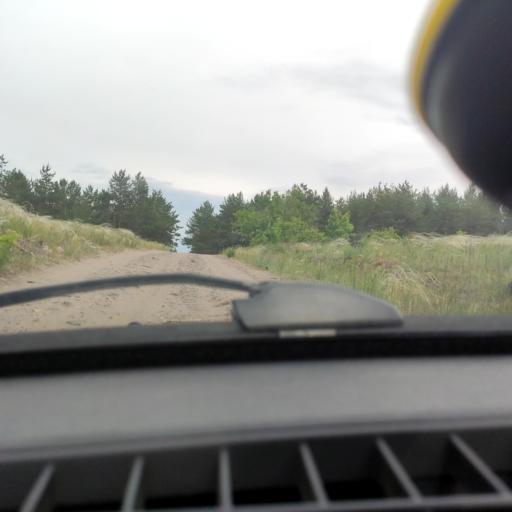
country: RU
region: Samara
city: Zhigulevsk
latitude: 53.5032
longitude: 49.5076
